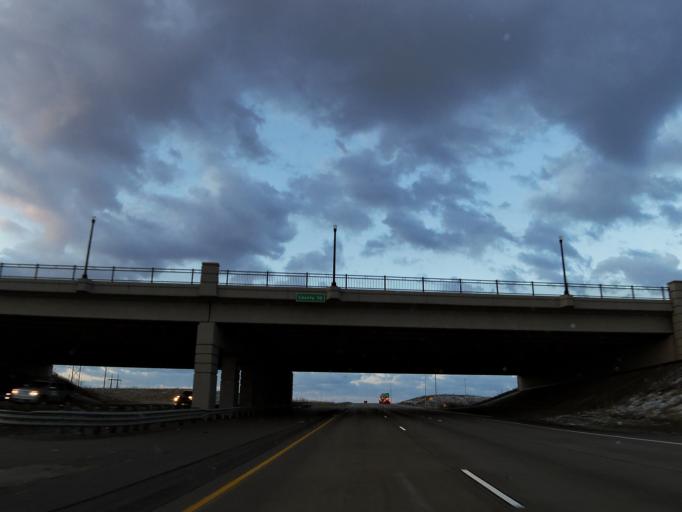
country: US
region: Minnesota
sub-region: Dakota County
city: Lakeville
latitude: 44.6459
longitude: -93.2961
